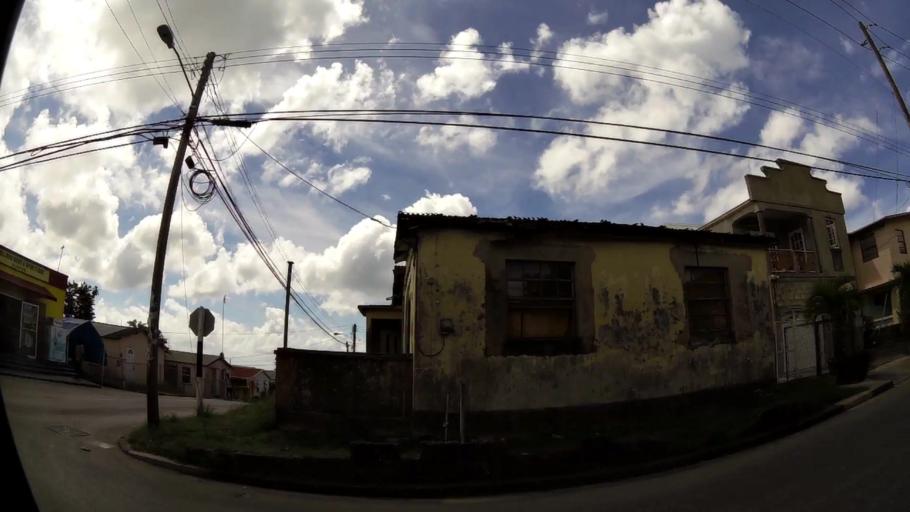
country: BB
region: Saint Michael
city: Bridgetown
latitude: 13.1347
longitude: -59.6212
